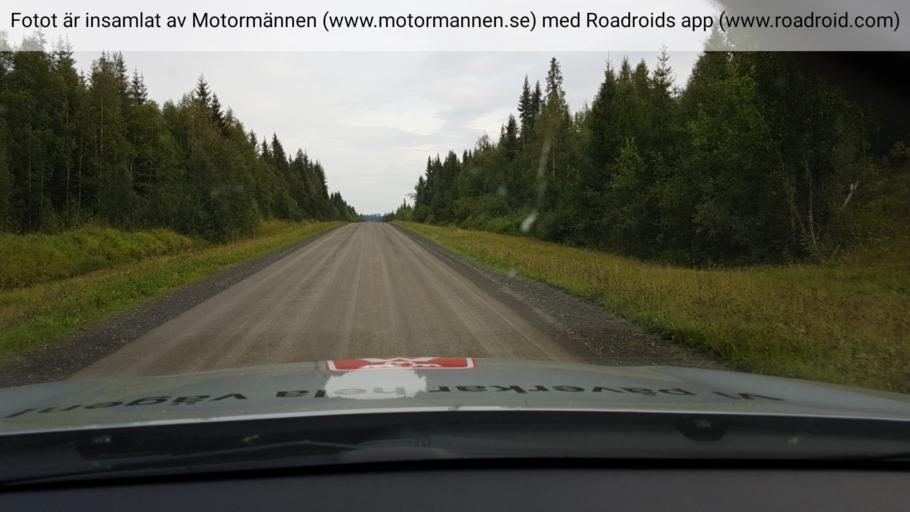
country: SE
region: Jaemtland
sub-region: OEstersunds Kommun
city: Lit
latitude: 63.6658
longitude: 14.8992
